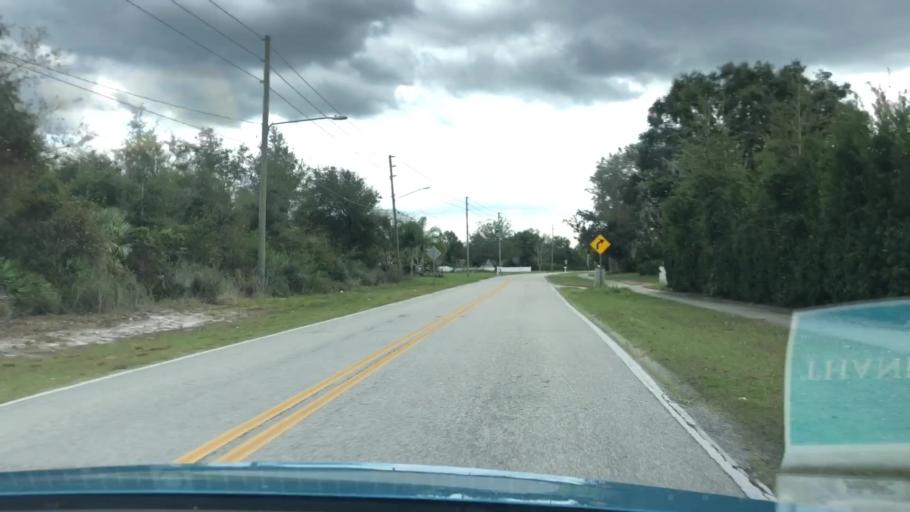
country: US
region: Florida
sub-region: Volusia County
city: Deltona
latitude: 28.8800
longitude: -81.2210
